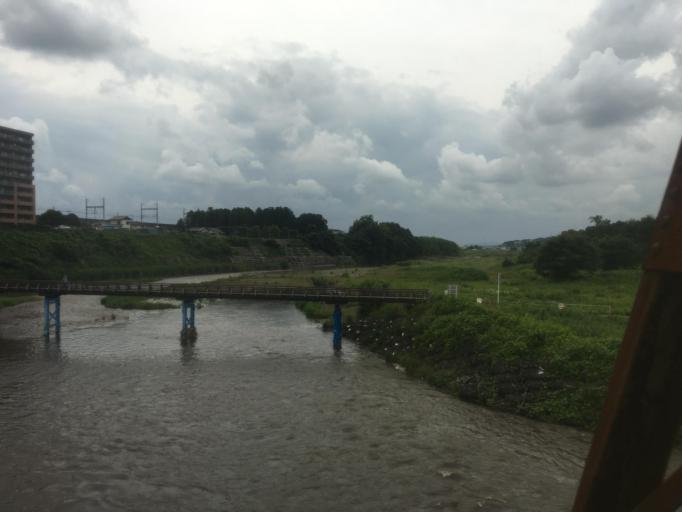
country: JP
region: Gunma
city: Takasaki
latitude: 36.3011
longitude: 139.0171
